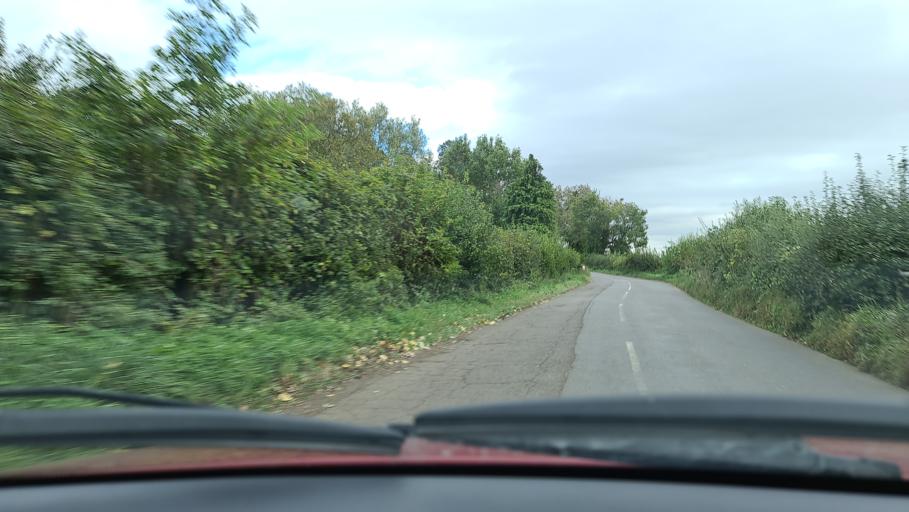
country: GB
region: England
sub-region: Oxfordshire
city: Adderbury
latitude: 52.0172
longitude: -1.2729
